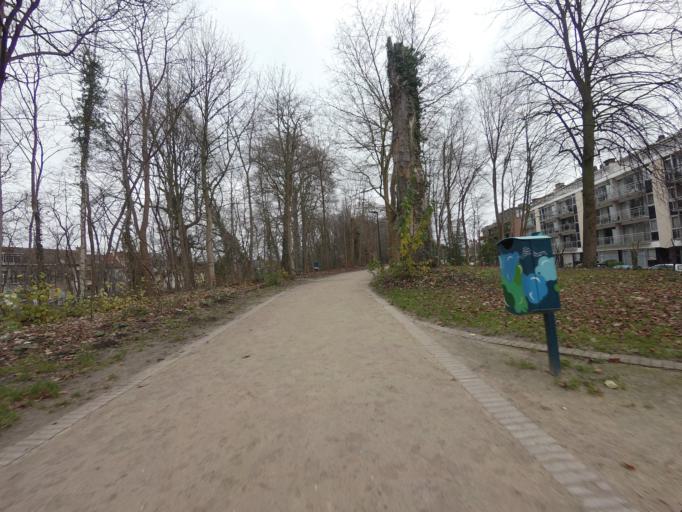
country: BE
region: Flanders
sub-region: Provincie Antwerpen
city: Lier
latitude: 51.1355
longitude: 4.5656
